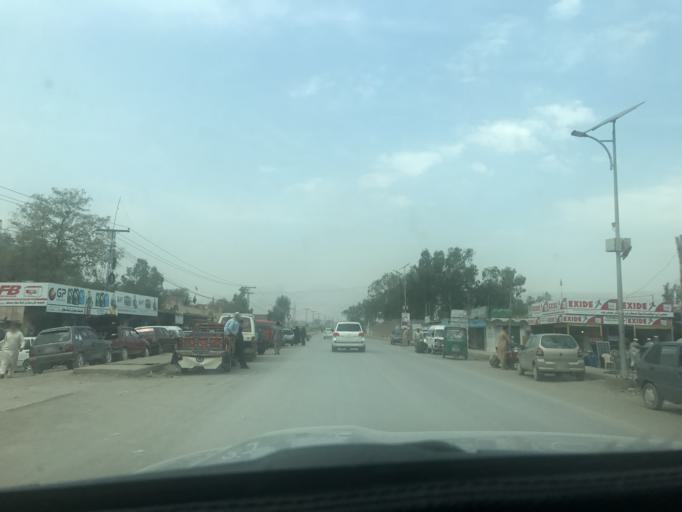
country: PK
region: Khyber Pakhtunkhwa
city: Peshawar
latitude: 34.0022
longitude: 71.3783
